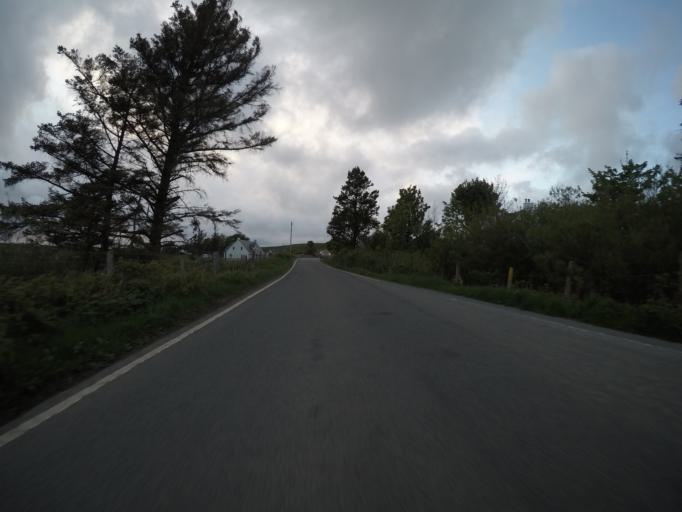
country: GB
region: Scotland
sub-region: Highland
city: Portree
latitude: 57.6198
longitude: -6.3730
